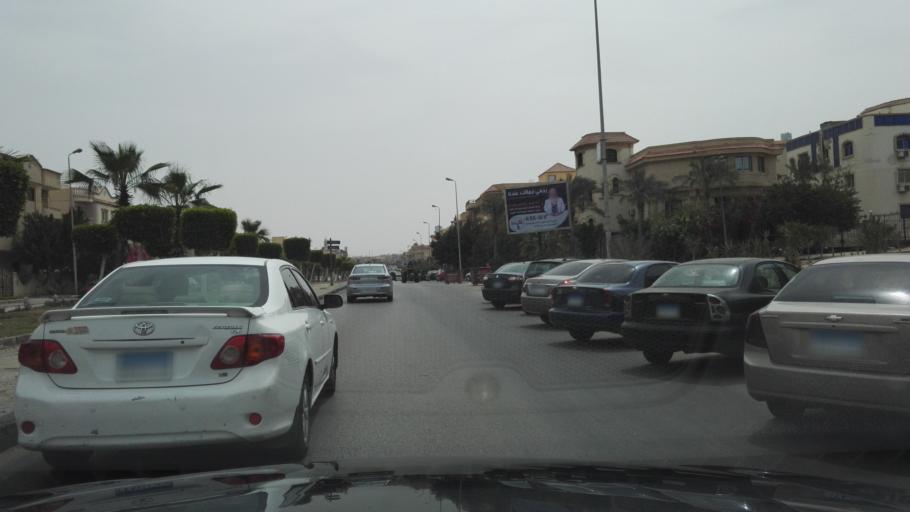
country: EG
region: Muhafazat al Qahirah
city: Cairo
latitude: 30.0064
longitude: 31.4143
